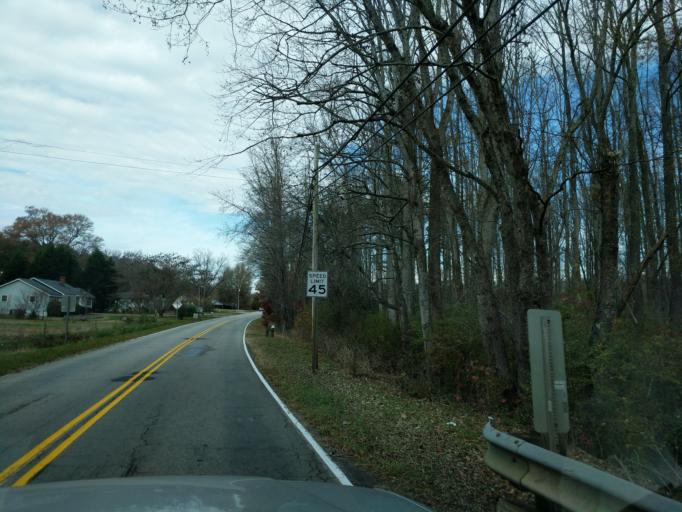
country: US
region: South Carolina
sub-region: Pickens County
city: Arial
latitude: 34.8451
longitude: -82.6443
